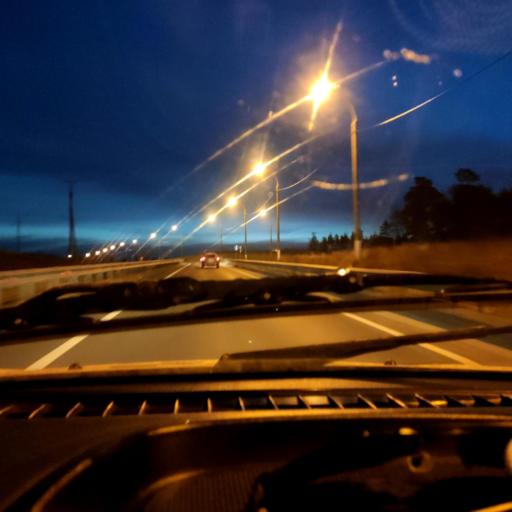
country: RU
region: Samara
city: Zhigulevsk
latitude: 53.4959
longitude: 49.5349
